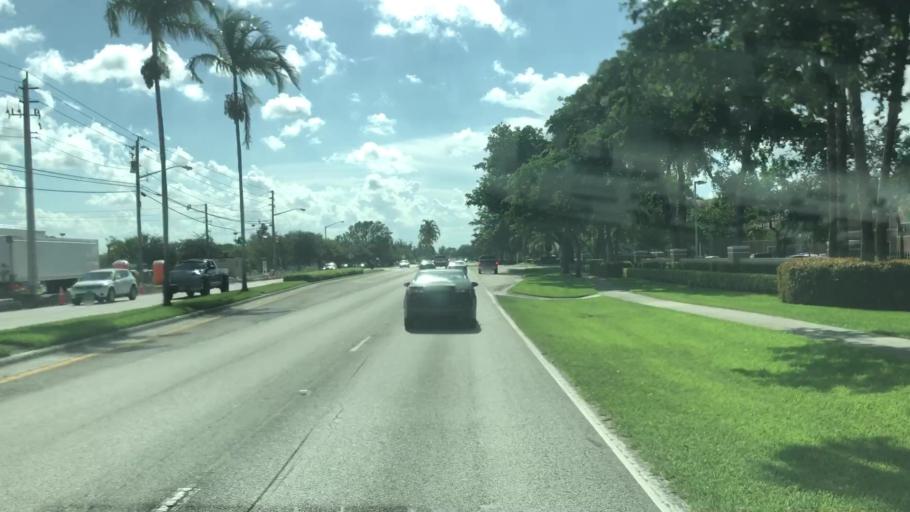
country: US
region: Florida
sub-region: Broward County
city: Parkland
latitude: 26.2870
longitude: -80.2447
